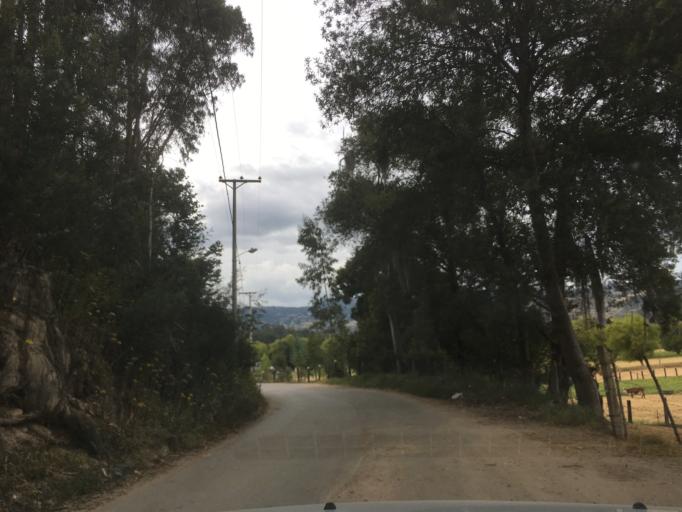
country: CO
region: Boyaca
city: Firavitoba
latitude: 5.6721
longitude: -73.0012
